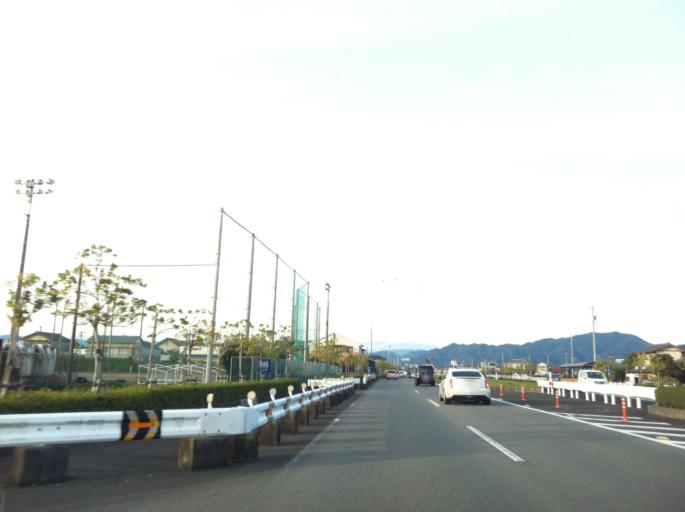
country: JP
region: Shizuoka
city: Yaizu
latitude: 34.8388
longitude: 138.3002
